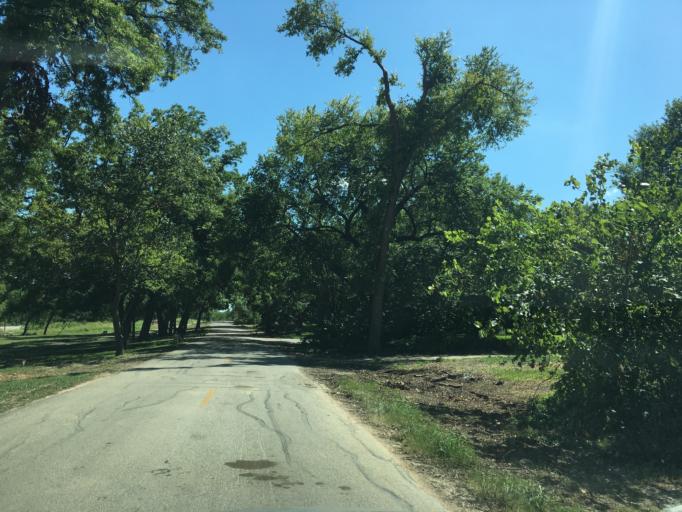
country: US
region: Texas
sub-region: Dallas County
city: Highland Park
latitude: 32.8396
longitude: -96.7093
